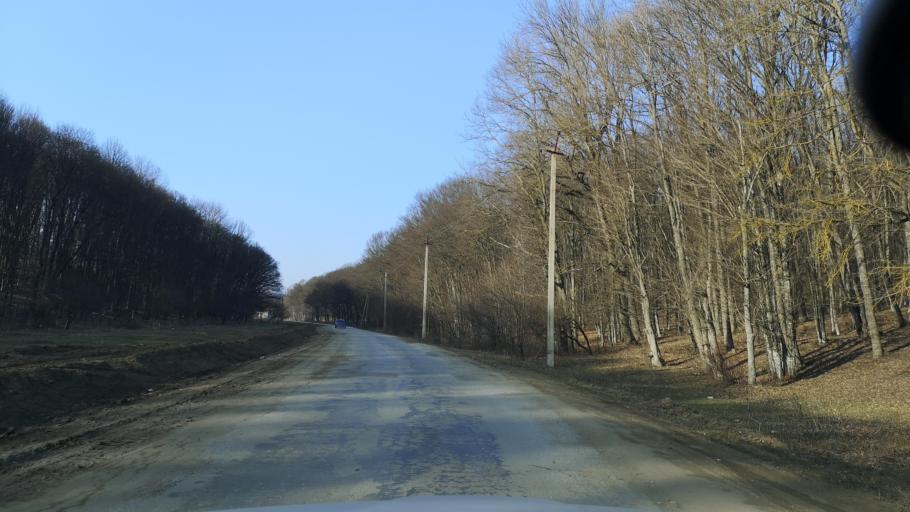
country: MD
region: Nisporeni
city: Nisporeni
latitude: 47.0845
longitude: 28.3219
